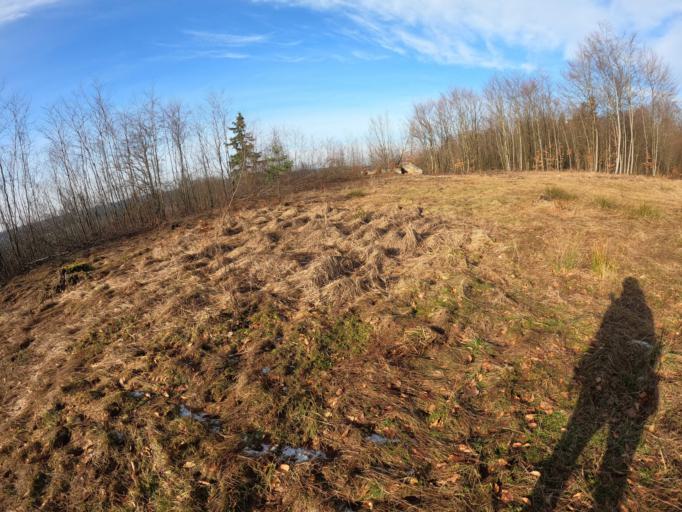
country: PL
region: West Pomeranian Voivodeship
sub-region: Powiat koszalinski
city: Polanow
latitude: 54.1225
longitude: 16.6992
